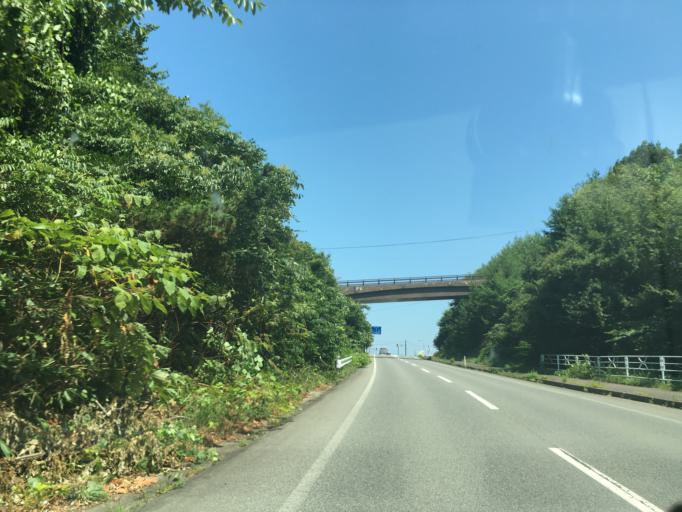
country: JP
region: Akita
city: Tenno
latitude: 39.9675
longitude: 139.7524
